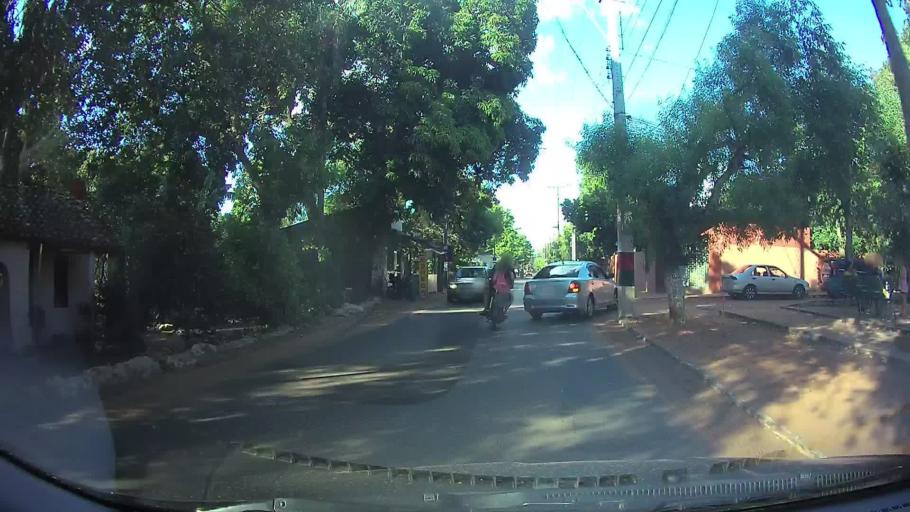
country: PY
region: Central
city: Aregua
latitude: -25.2891
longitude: -57.4400
